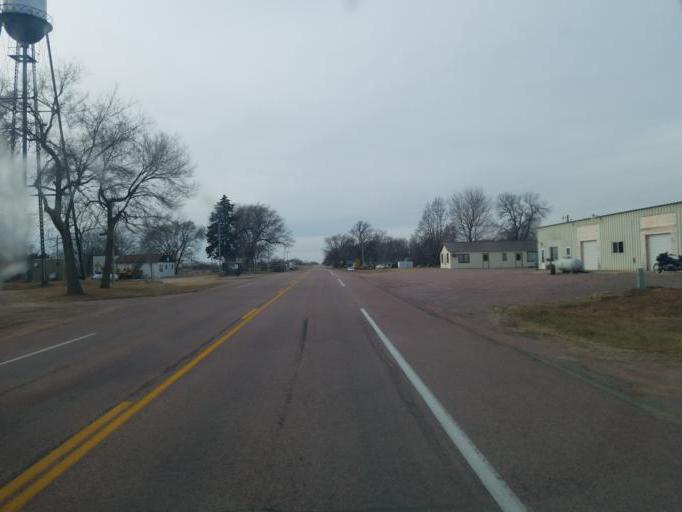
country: US
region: Nebraska
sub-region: Antelope County
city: Neligh
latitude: 42.3353
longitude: -98.1227
